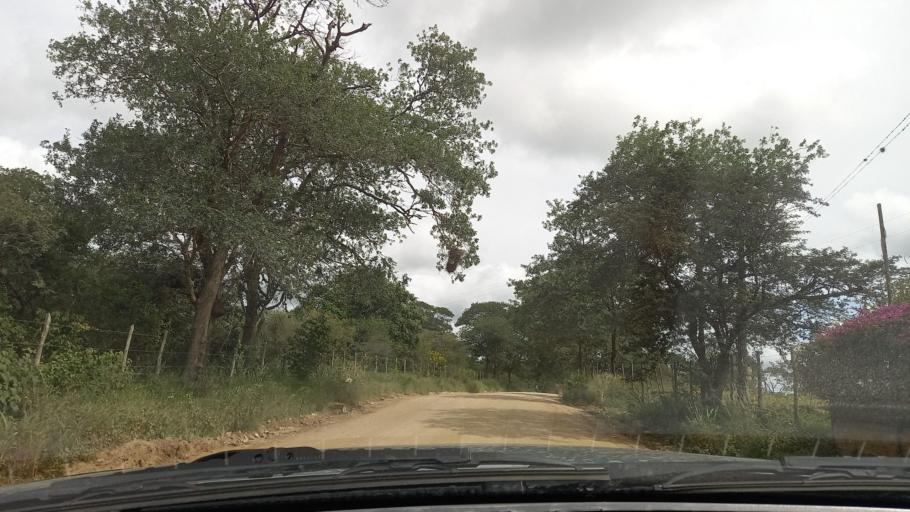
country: BR
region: Pernambuco
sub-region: Gravata
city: Gravata
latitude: -8.1805
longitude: -35.5898
